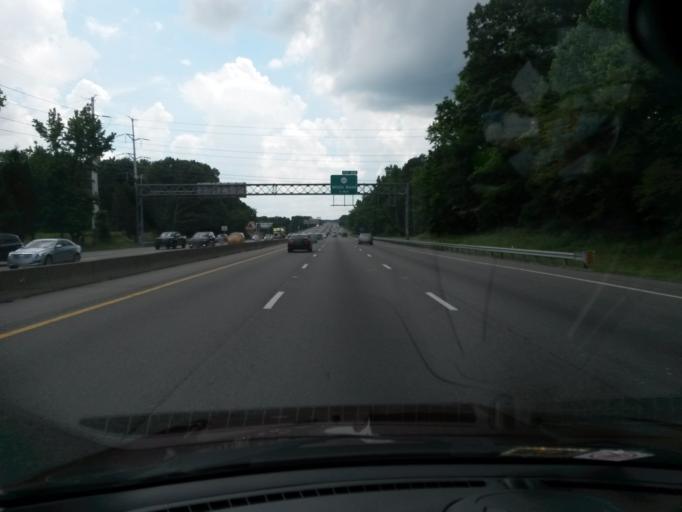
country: US
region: Virginia
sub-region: Chesterfield County
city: Bellwood
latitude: 37.4182
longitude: -77.4277
